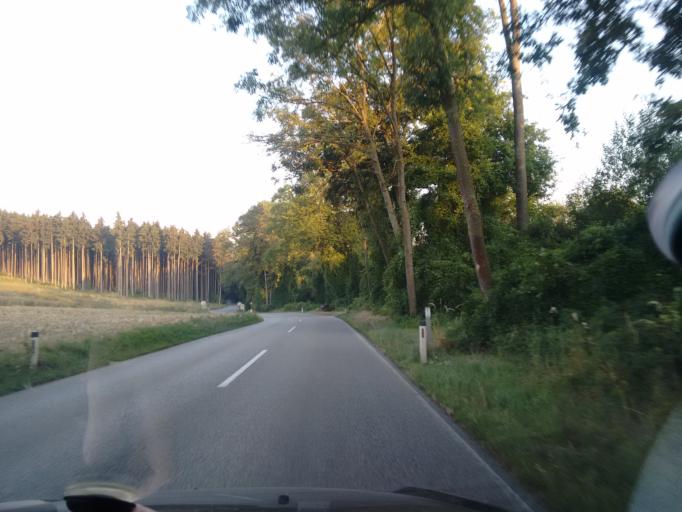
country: AT
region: Upper Austria
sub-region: Wels-Land
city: Gunskirchen
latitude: 48.1839
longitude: 13.9668
